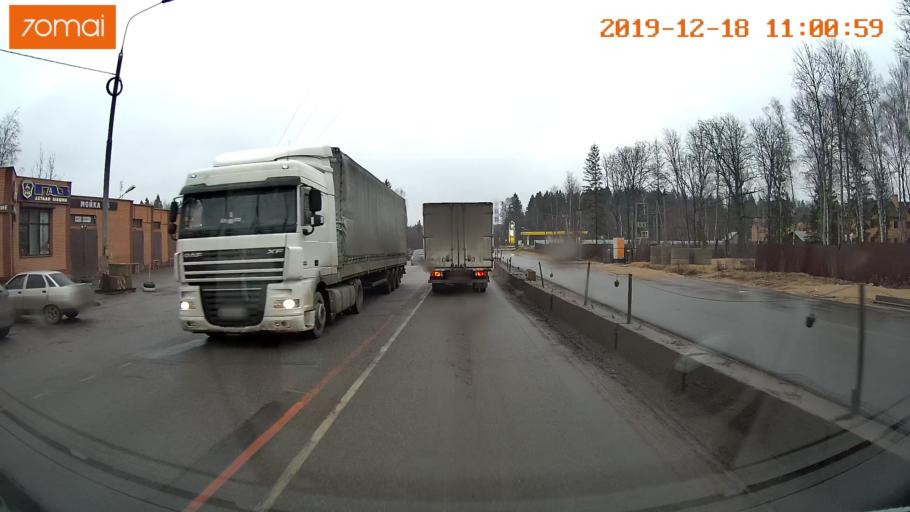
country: RU
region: Moskovskaya
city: Golitsyno
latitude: 55.5678
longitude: 36.9968
